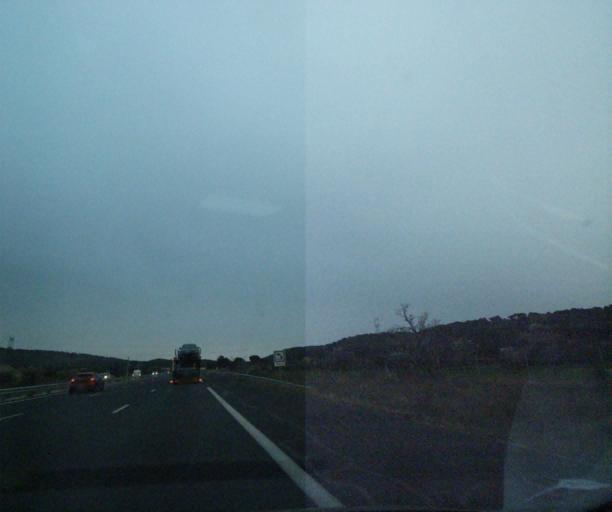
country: FR
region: Provence-Alpes-Cote d'Azur
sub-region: Departement des Bouches-du-Rhone
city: Coudoux
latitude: 43.5566
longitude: 5.2592
